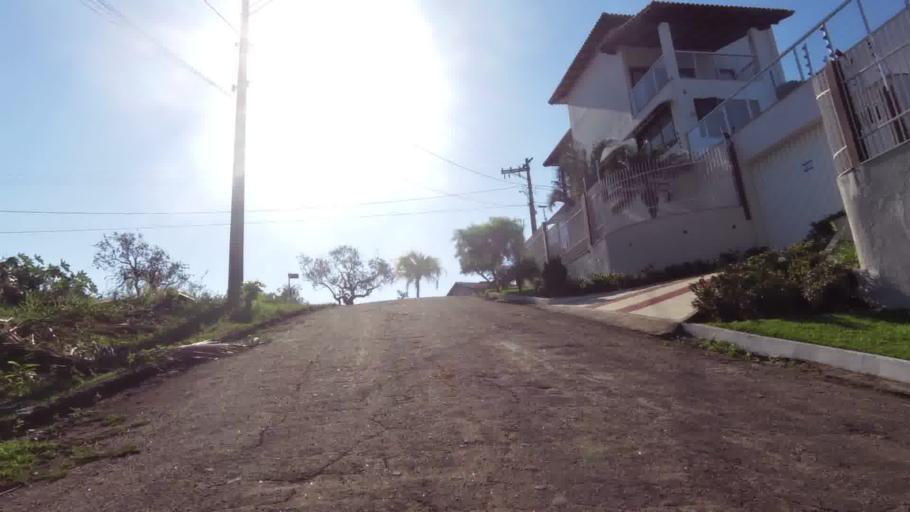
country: BR
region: Espirito Santo
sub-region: Guarapari
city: Guarapari
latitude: -20.7383
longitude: -40.5564
